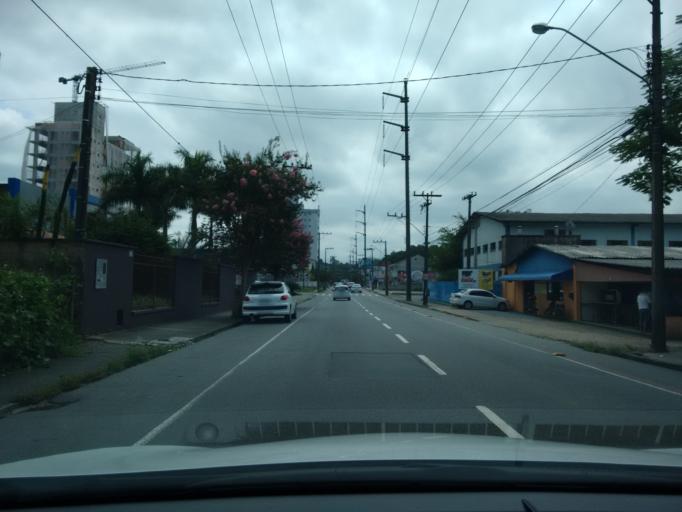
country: BR
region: Santa Catarina
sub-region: Jaragua Do Sul
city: Jaragua do Sul
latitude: -26.4970
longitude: -49.0828
